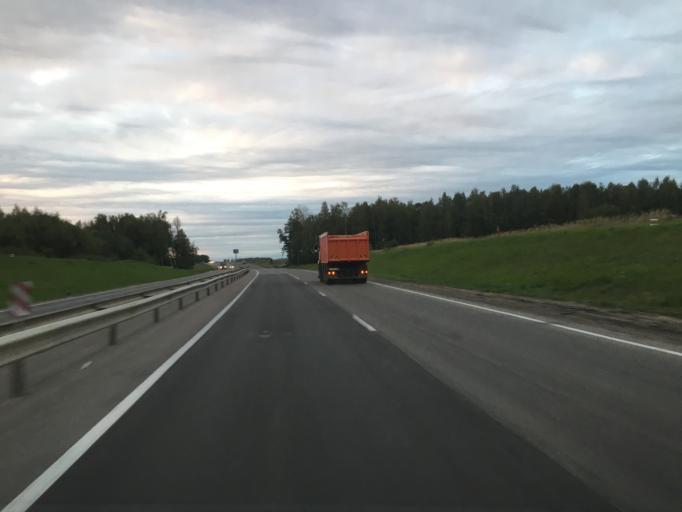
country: RU
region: Kaluga
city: Kaluga
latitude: 54.6100
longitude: 36.3091
